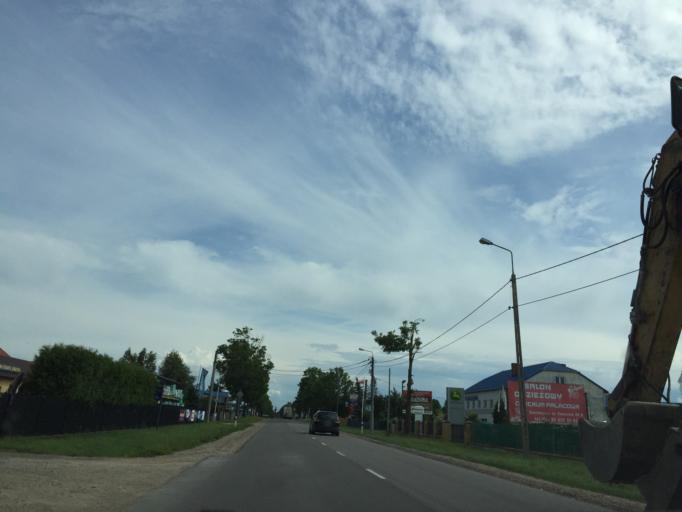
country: PL
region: Podlasie
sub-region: Powiat siemiatycki
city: Siemiatycze
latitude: 52.4391
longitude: 22.8527
